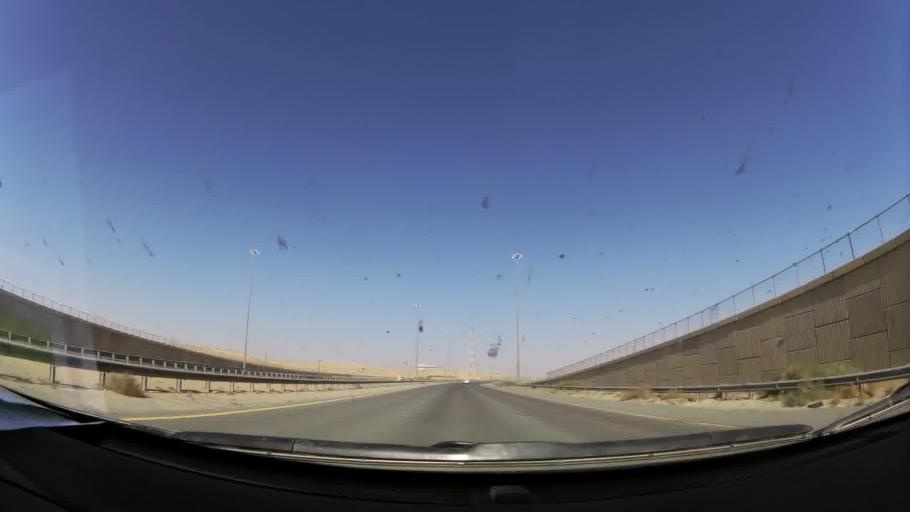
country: KW
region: Muhafazat al Jahra'
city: Al Jahra'
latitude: 29.4766
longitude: 47.7692
